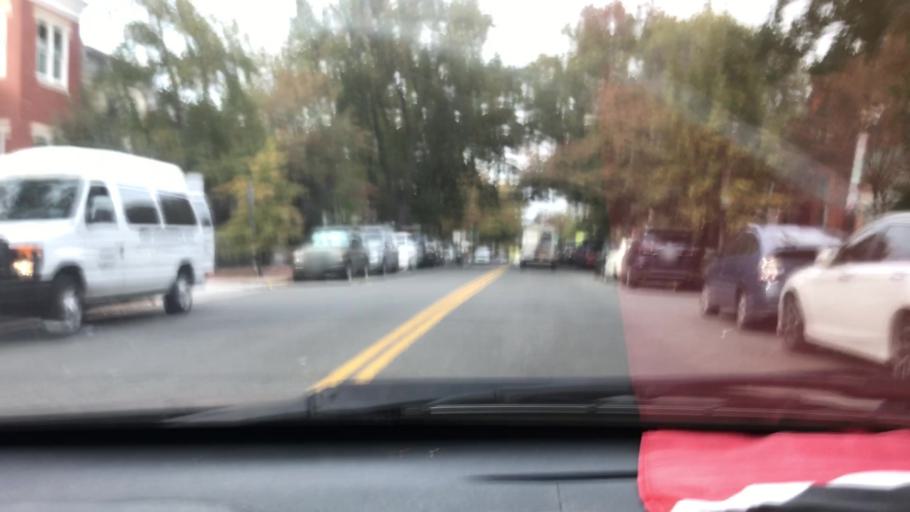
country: US
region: Washington, D.C.
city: Washington, D.C.
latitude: 38.8939
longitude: -76.9949
